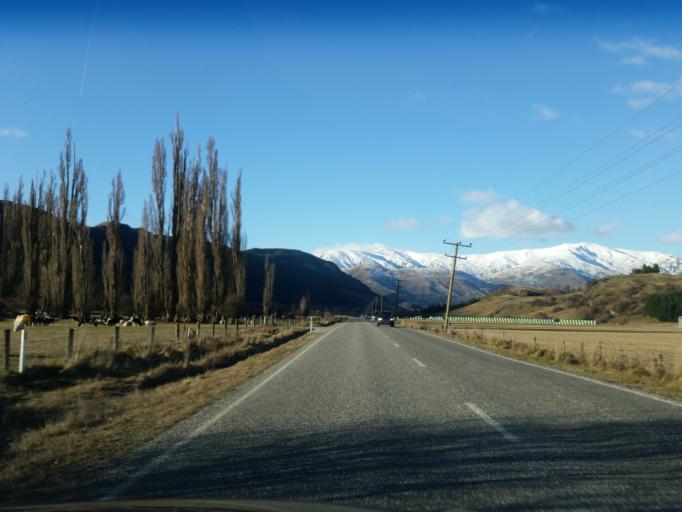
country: NZ
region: Otago
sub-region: Queenstown-Lakes District
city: Arrowtown
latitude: -44.9525
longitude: 168.7483
